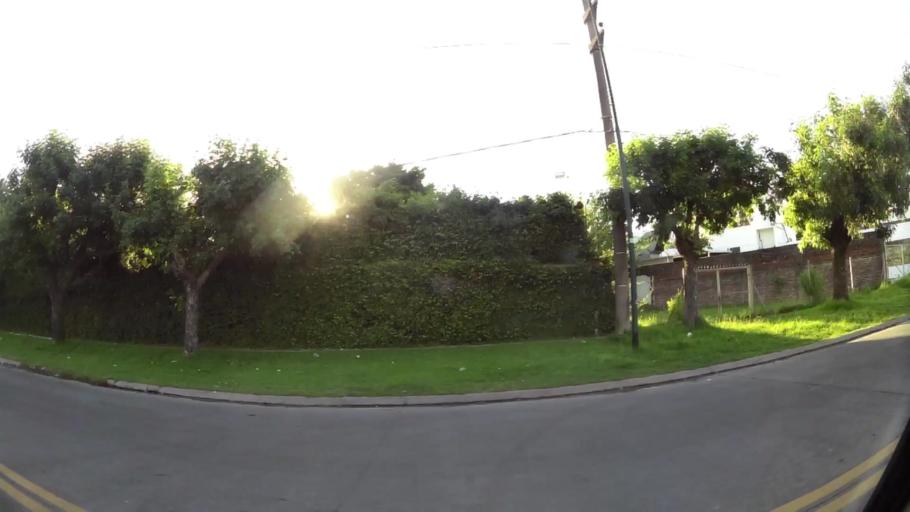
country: AR
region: Buenos Aires
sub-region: Partido de San Isidro
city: San Isidro
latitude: -34.4666
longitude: -58.5550
